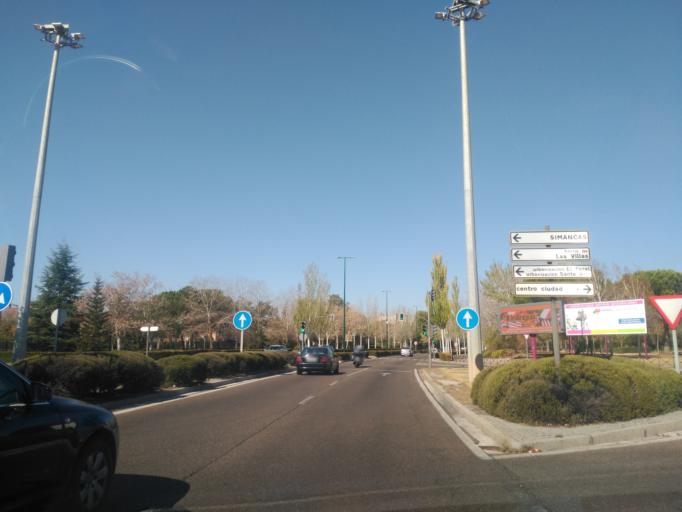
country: ES
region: Castille and Leon
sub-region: Provincia de Valladolid
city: Valladolid
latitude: 41.6233
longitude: -4.7526
